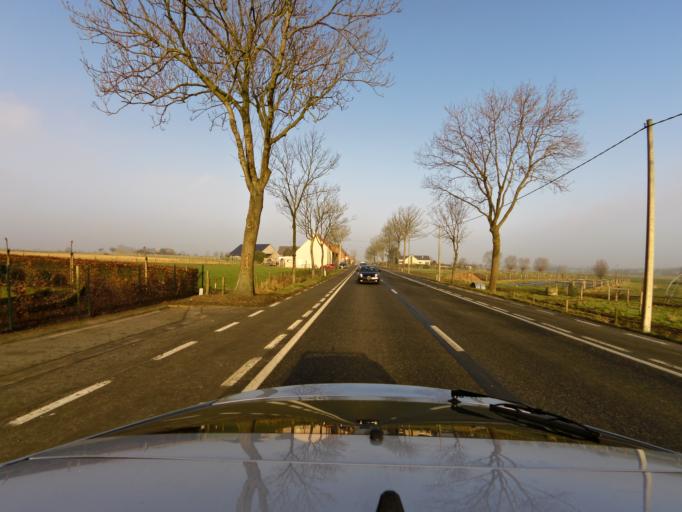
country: BE
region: Flanders
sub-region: Provincie West-Vlaanderen
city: Ichtegem
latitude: 51.0926
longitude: 3.0462
